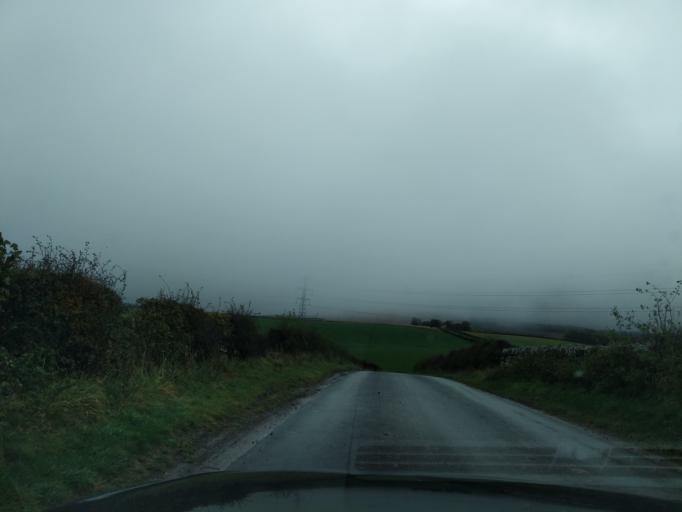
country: GB
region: Scotland
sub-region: East Lothian
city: Dunbar
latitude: 55.9431
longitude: -2.4047
